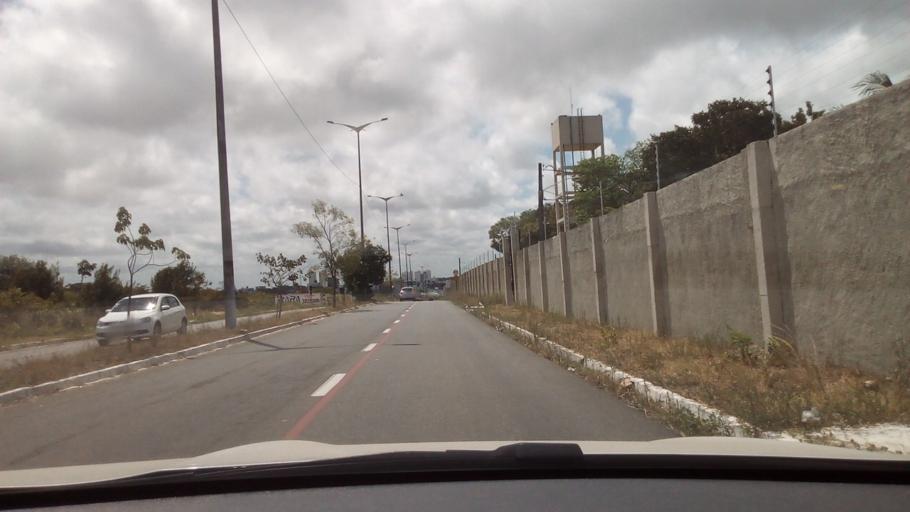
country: BR
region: Paraiba
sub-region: Joao Pessoa
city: Joao Pessoa
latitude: -7.1415
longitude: -34.8226
